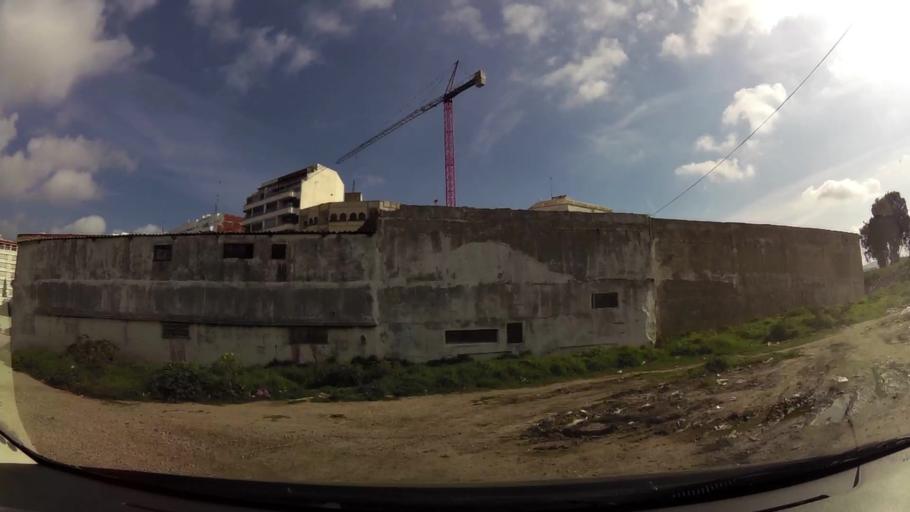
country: MA
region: Tanger-Tetouan
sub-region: Tanger-Assilah
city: Tangier
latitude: 35.7713
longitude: -5.7990
